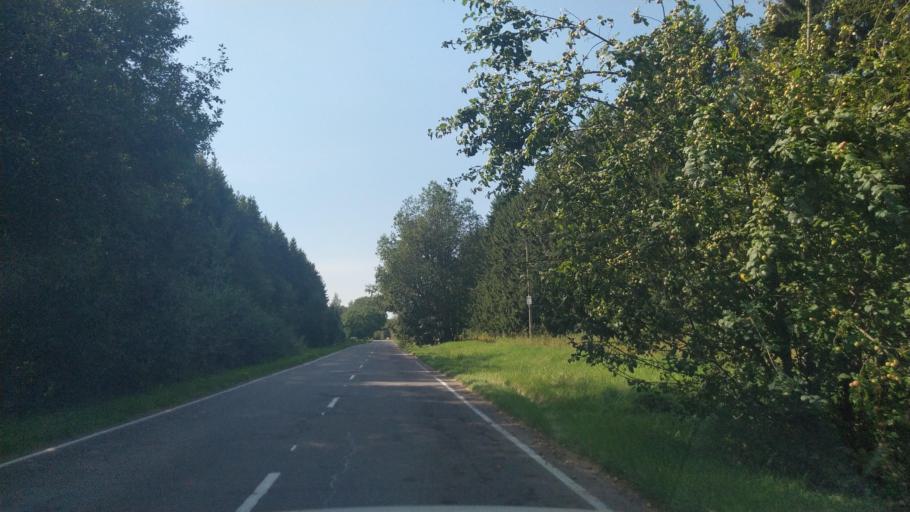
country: RU
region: Leningrad
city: Siverskiy
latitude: 59.3003
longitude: 30.0772
